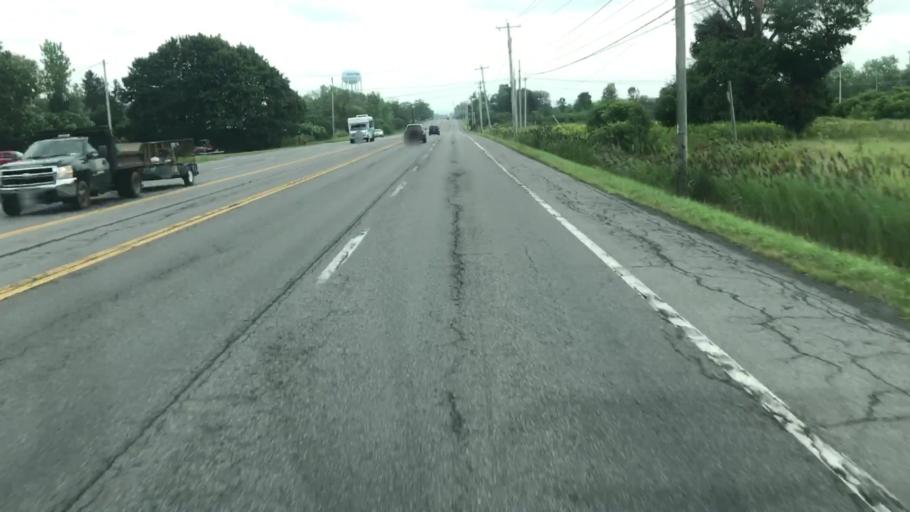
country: US
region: New York
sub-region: Onondaga County
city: Liverpool
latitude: 43.1287
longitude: -76.1866
